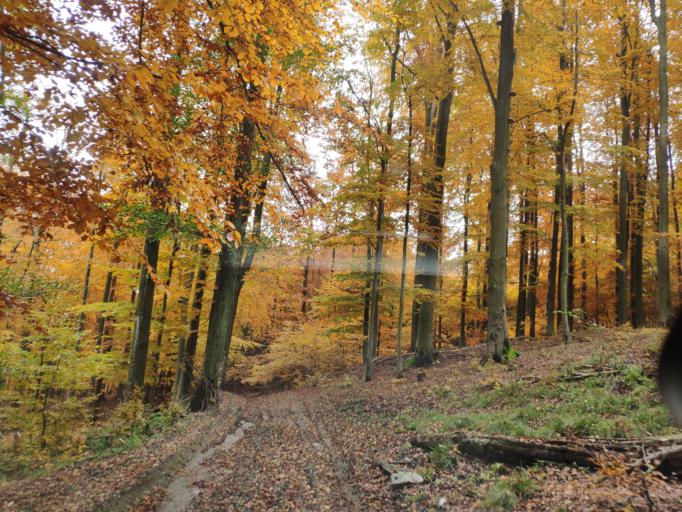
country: SK
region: Kosicky
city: Moldava nad Bodvou
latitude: 48.7339
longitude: 21.0168
